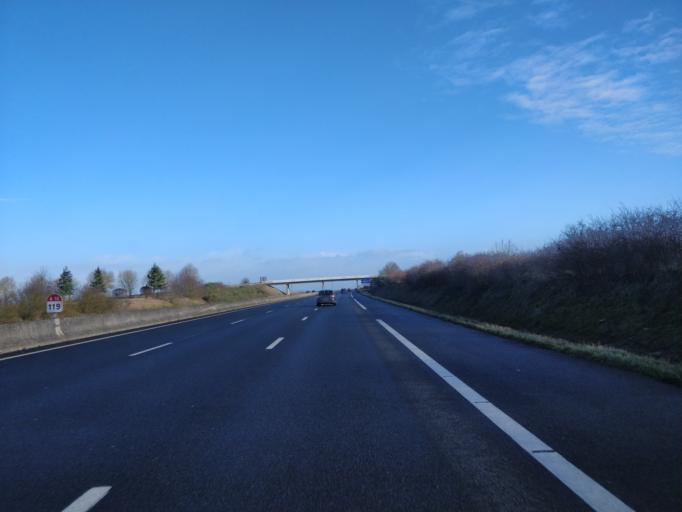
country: FR
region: Centre
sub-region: Departement du Loiret
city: Beaugency
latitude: 47.8100
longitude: 1.6251
